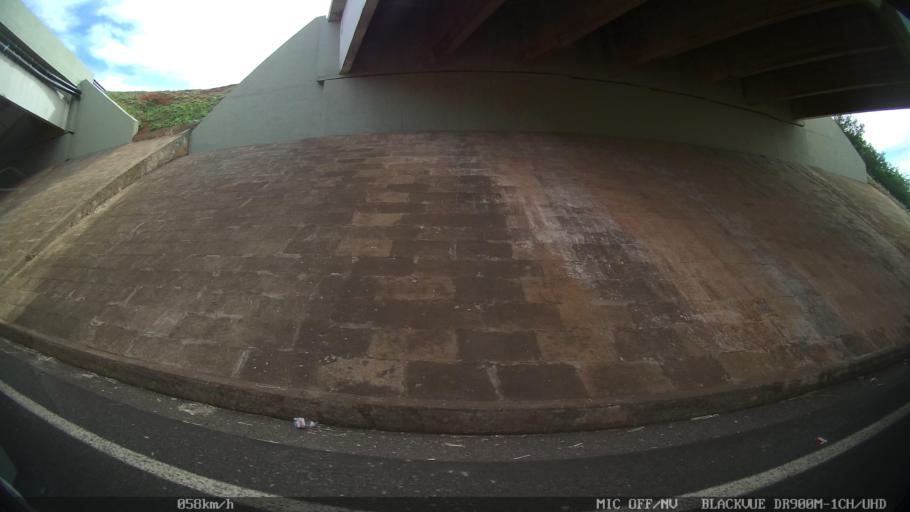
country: BR
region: Sao Paulo
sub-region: Taquaritinga
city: Taquaritinga
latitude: -21.4760
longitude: -48.5995
